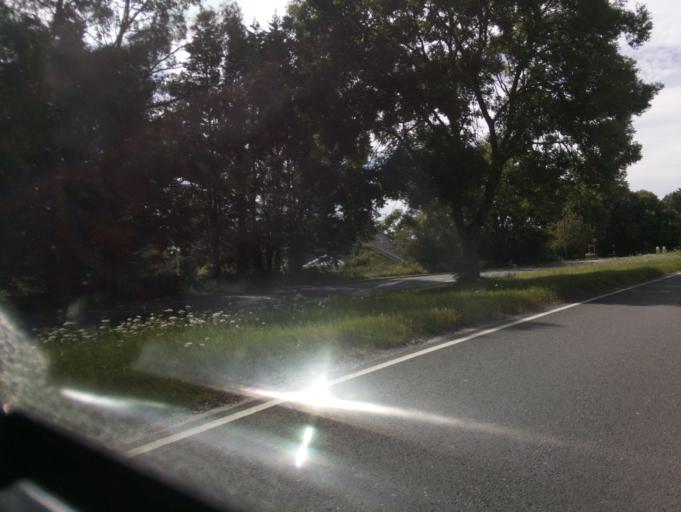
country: GB
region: England
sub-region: Dorset
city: Dorchester
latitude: 50.7408
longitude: -2.4883
